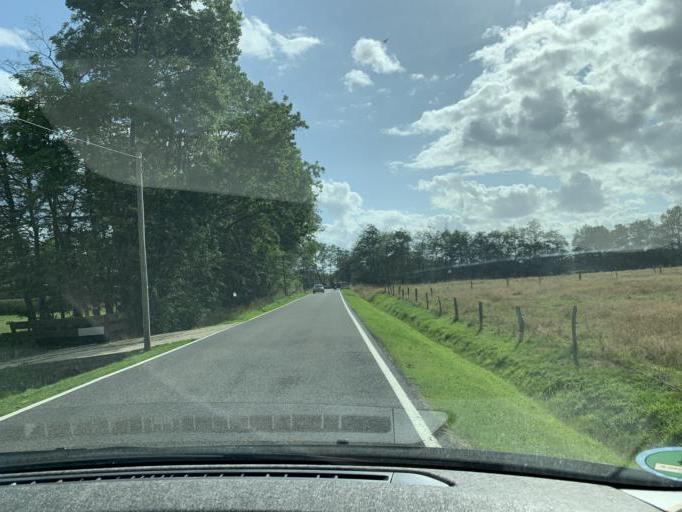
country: DE
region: North Rhine-Westphalia
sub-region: Regierungsbezirk Koln
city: Simmerath
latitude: 50.6070
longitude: 6.2636
